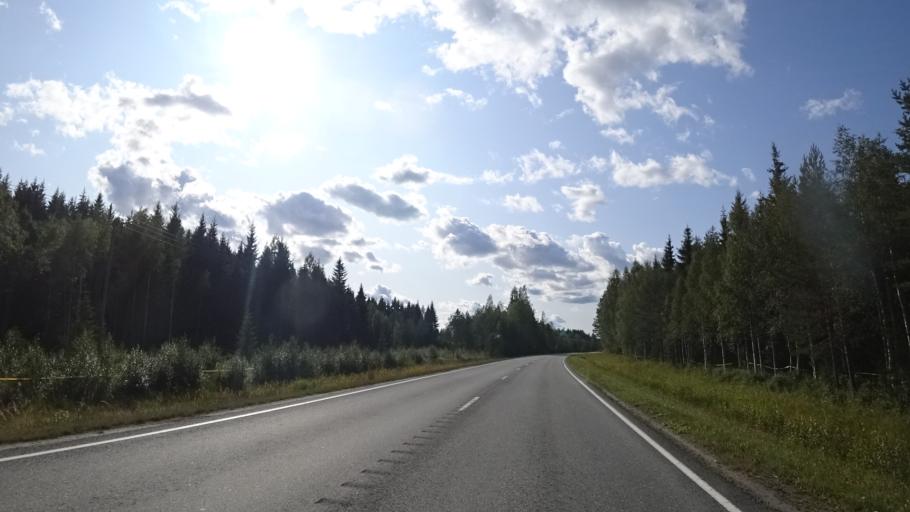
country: FI
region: North Karelia
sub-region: Keski-Karjala
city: Kitee
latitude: 62.0951
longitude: 30.0923
